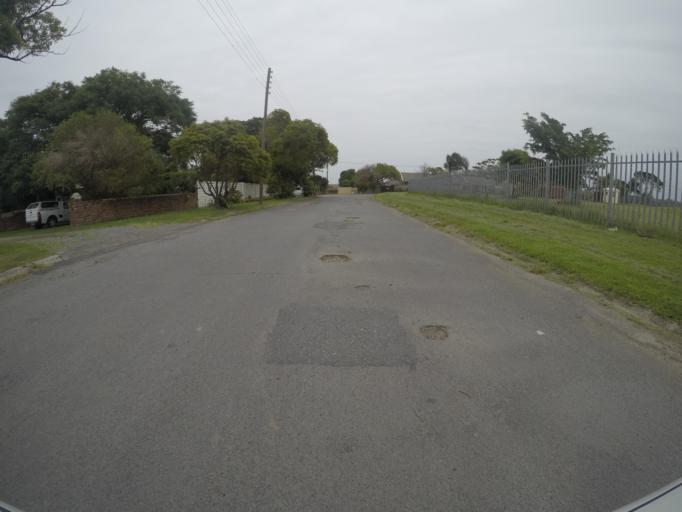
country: ZA
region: Eastern Cape
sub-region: Buffalo City Metropolitan Municipality
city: East London
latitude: -32.9683
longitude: 27.9354
